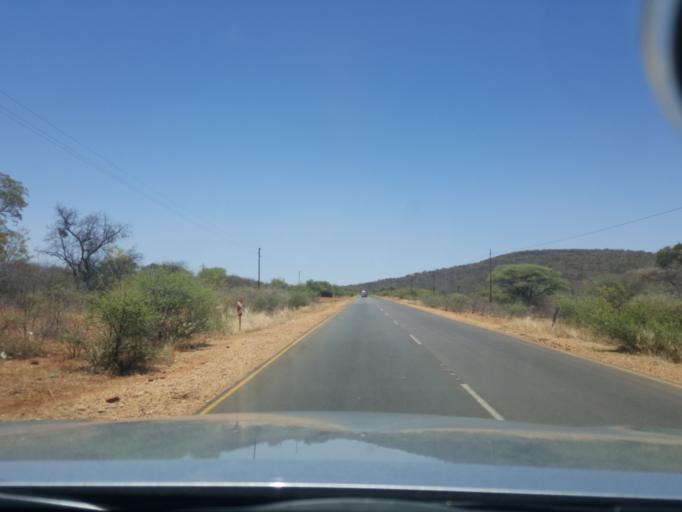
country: ZA
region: North-West
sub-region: Ngaka Modiri Molema District Municipality
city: Zeerust
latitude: -25.3811
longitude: 25.9350
